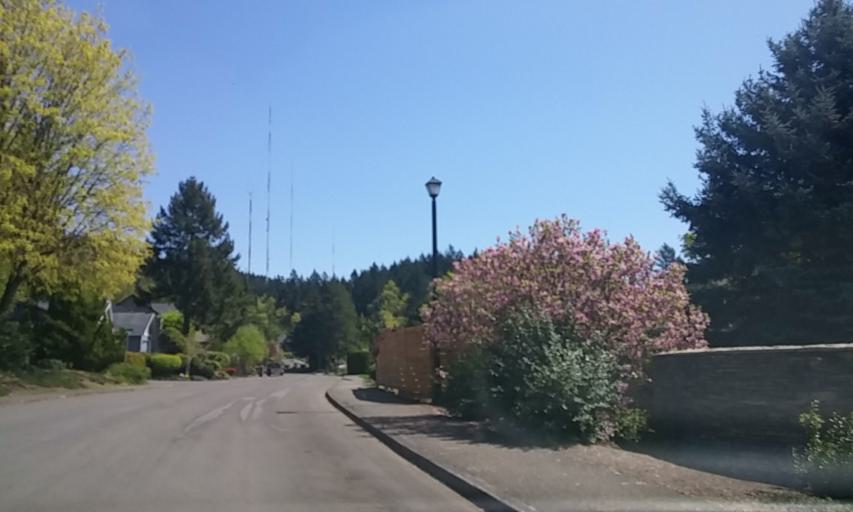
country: US
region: Oregon
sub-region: Washington County
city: West Haven
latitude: 45.5241
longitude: -122.7669
